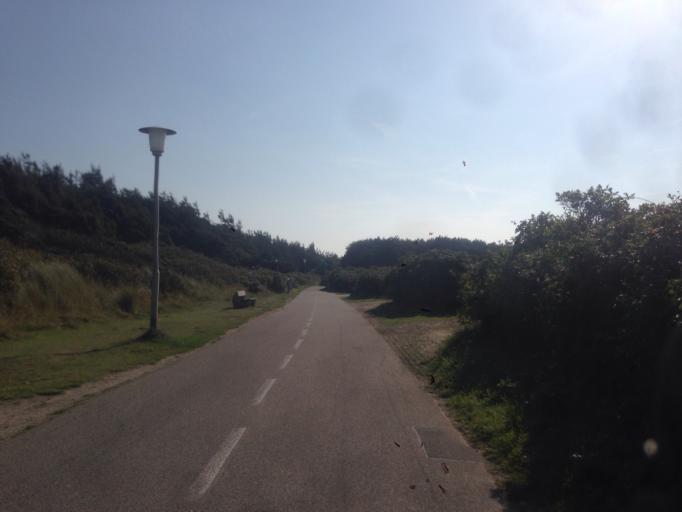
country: DE
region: Schleswig-Holstein
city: Westerland
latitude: 54.9243
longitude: 8.3100
